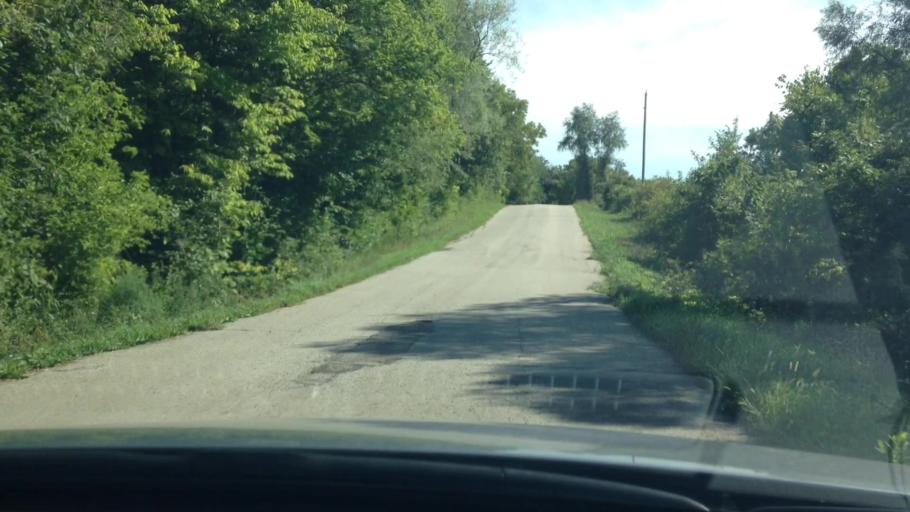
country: US
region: Missouri
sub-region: Platte County
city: Weatherby Lake
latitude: 39.3341
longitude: -94.6675
